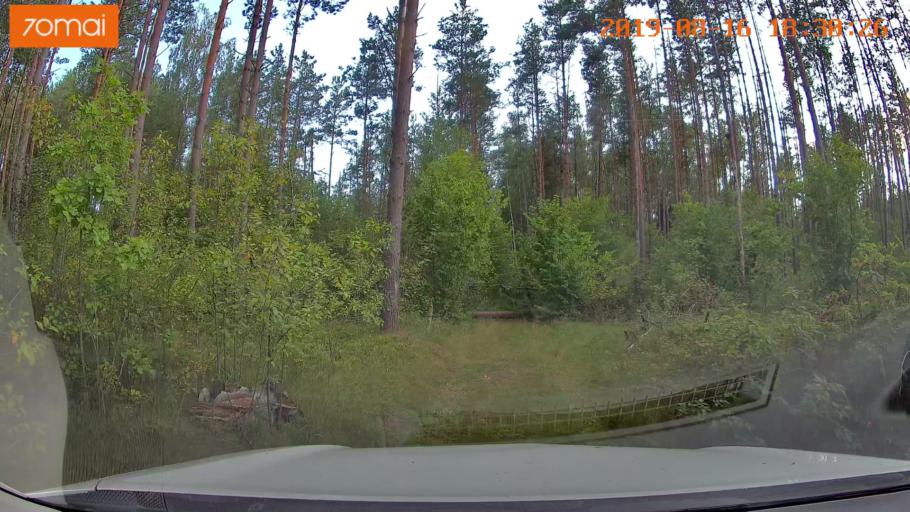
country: BY
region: Mogilev
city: Asipovichy
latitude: 53.1974
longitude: 28.6383
